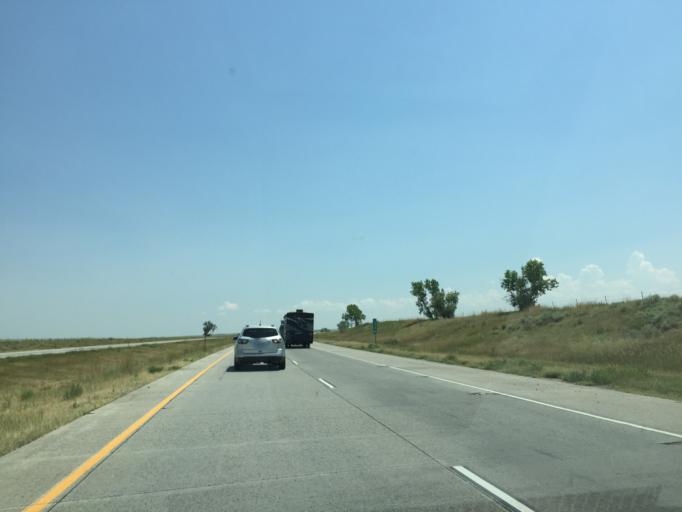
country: US
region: Colorado
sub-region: Arapahoe County
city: Byers
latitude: 39.6656
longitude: -104.0877
